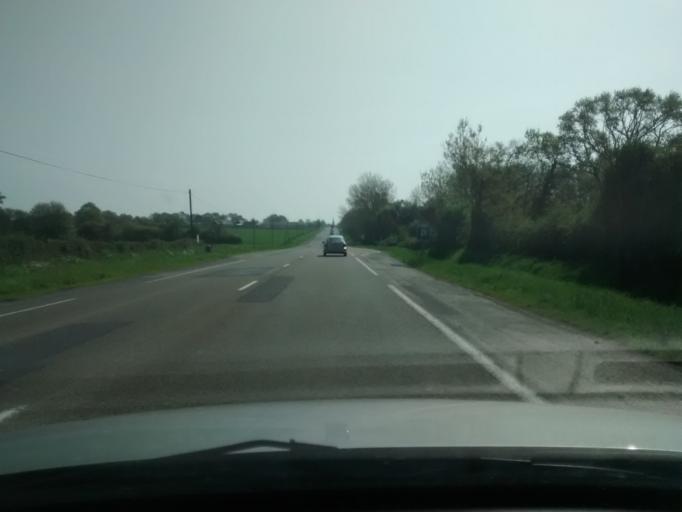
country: FR
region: Pays de la Loire
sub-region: Departement de la Mayenne
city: Soulge-sur-Ouette
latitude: 48.0617
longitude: -0.5908
